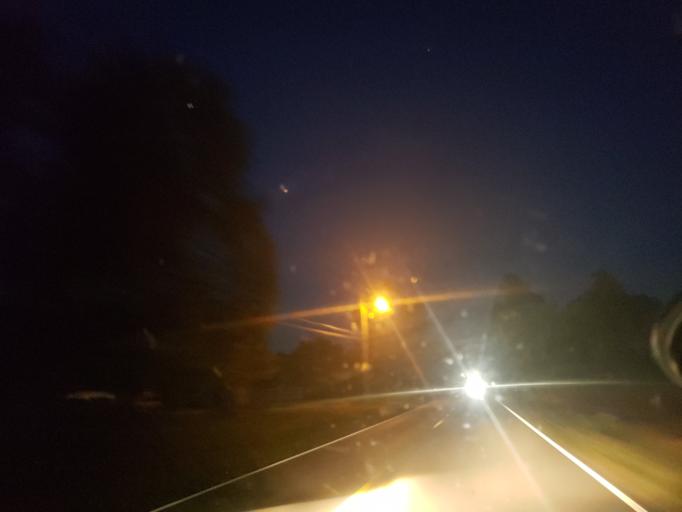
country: US
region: Alabama
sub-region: Madison County
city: Hazel Green
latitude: 34.9769
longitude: -86.6361
